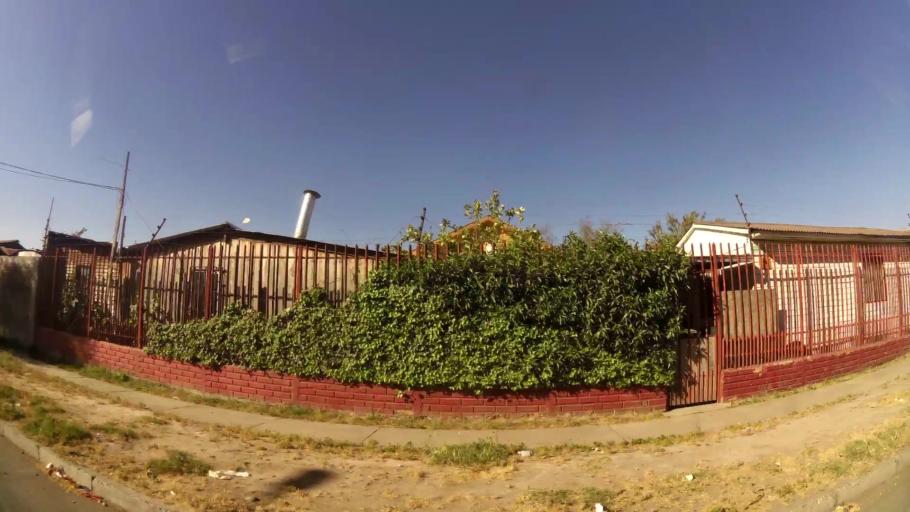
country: CL
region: Santiago Metropolitan
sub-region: Provincia de Maipo
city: San Bernardo
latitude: -33.5908
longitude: -70.6832
